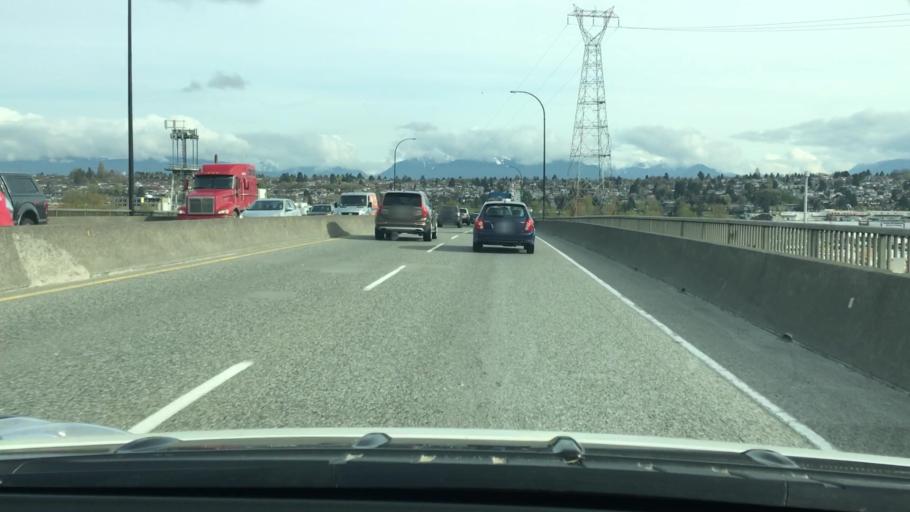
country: CA
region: British Columbia
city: Vancouver
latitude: 49.2013
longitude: -123.0774
